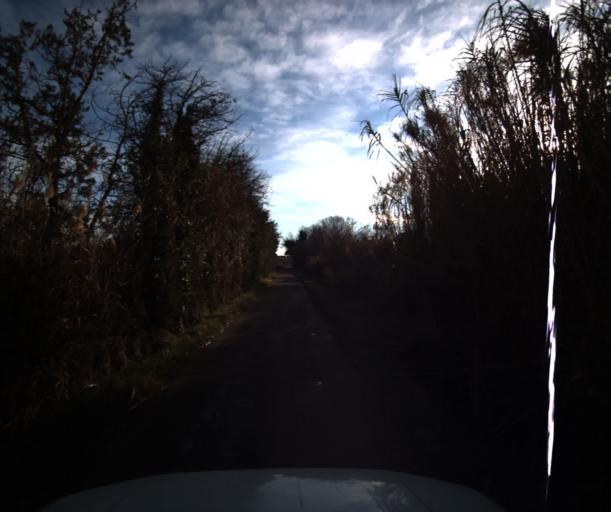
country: FR
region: Provence-Alpes-Cote d'Azur
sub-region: Departement du Vaucluse
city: Pertuis
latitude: 43.6707
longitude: 5.4933
